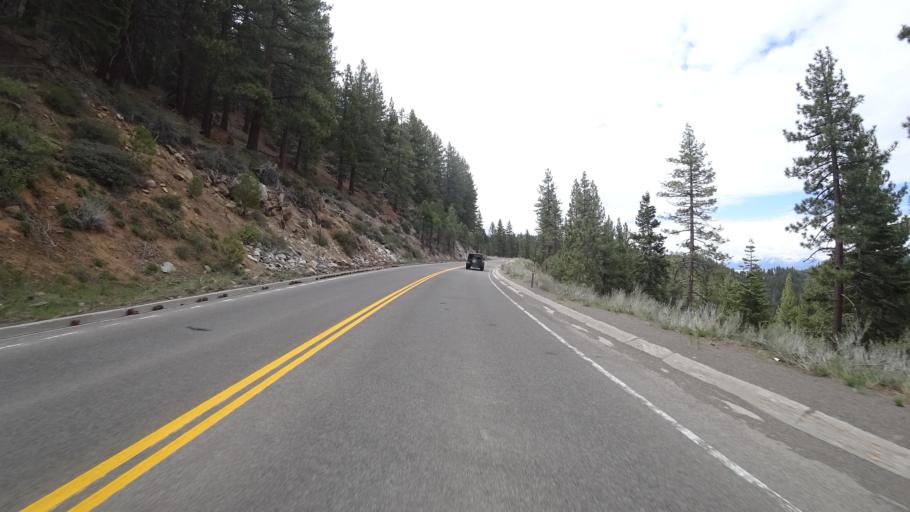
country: US
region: Nevada
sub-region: Washoe County
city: Incline Village
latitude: 39.1268
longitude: -119.9303
